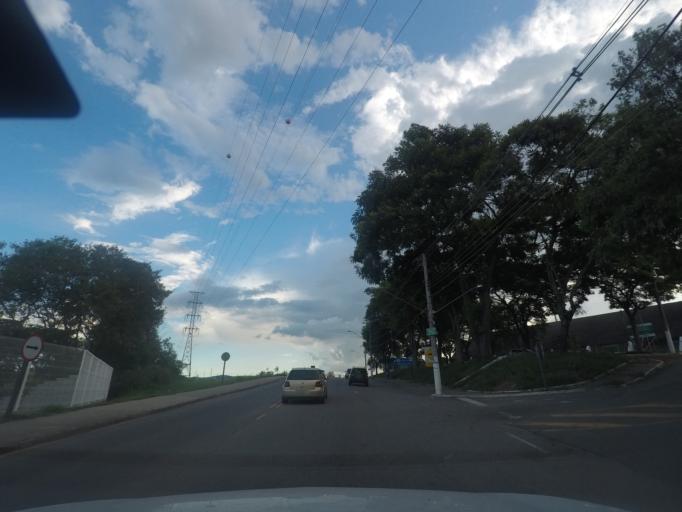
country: BR
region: Sao Paulo
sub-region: Cacapava
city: Cacapava
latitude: -23.1146
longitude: -45.7084
